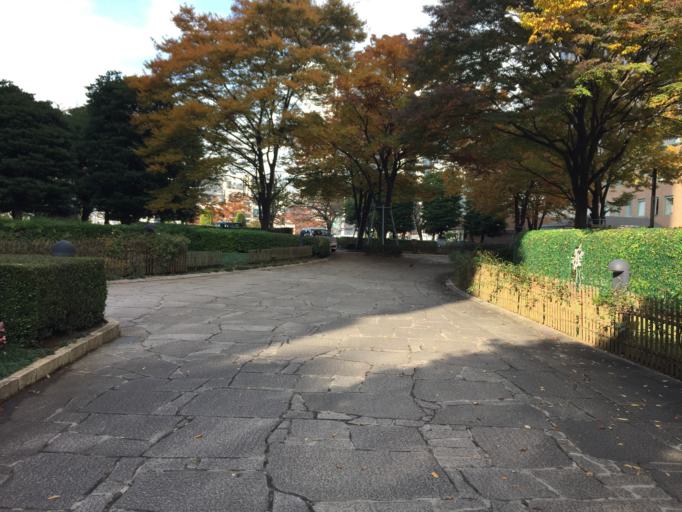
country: JP
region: Tokyo
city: Tokyo
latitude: 35.6696
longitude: 139.7838
